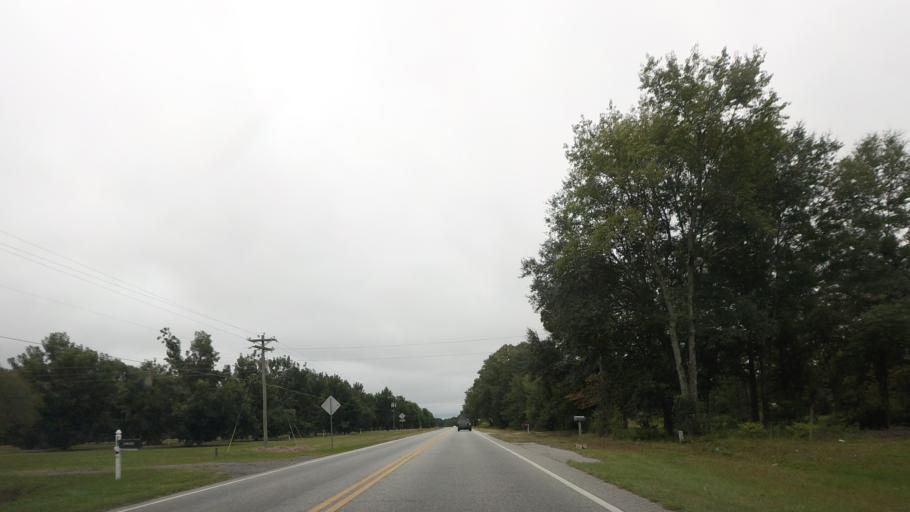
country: US
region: Georgia
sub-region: Berrien County
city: Ray City
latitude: 31.0387
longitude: -83.1977
